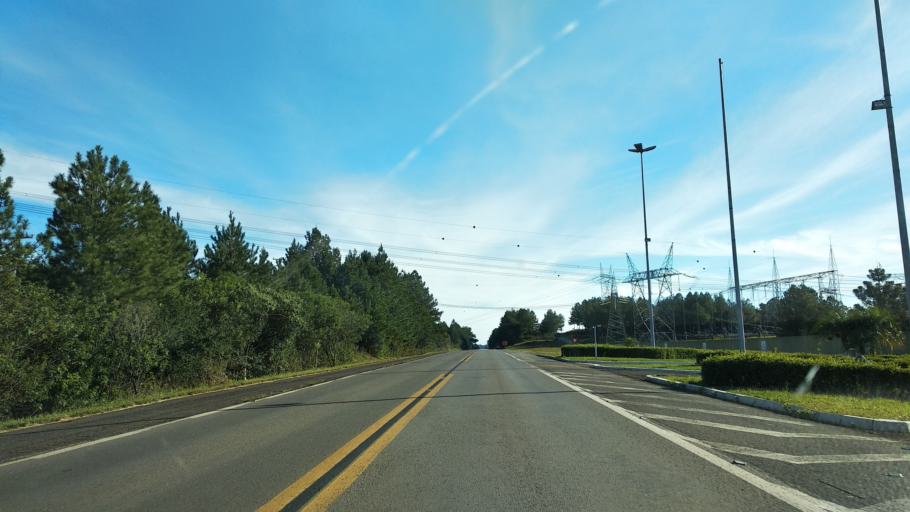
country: BR
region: Santa Catarina
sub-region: Celso Ramos
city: Celso Ramos
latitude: -27.5411
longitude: -51.4155
